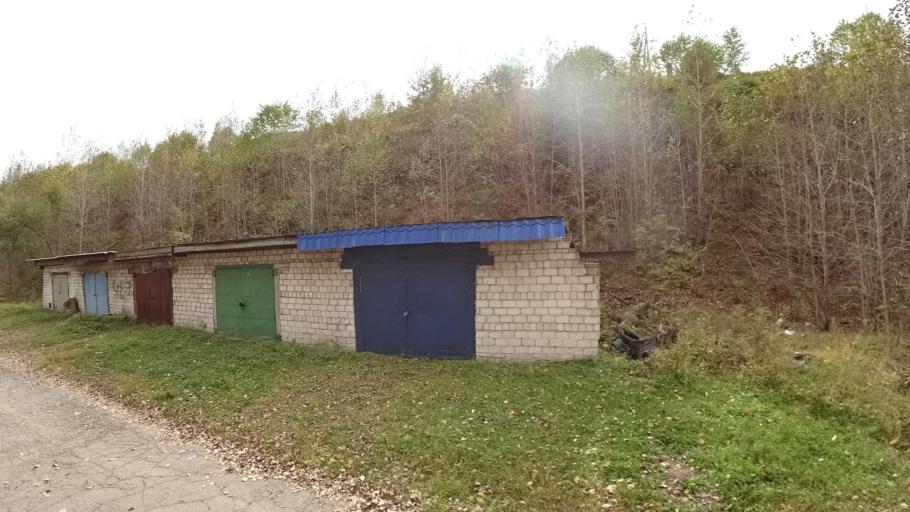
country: RU
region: Jewish Autonomous Oblast
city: Khingansk
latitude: 49.1245
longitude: 131.1976
